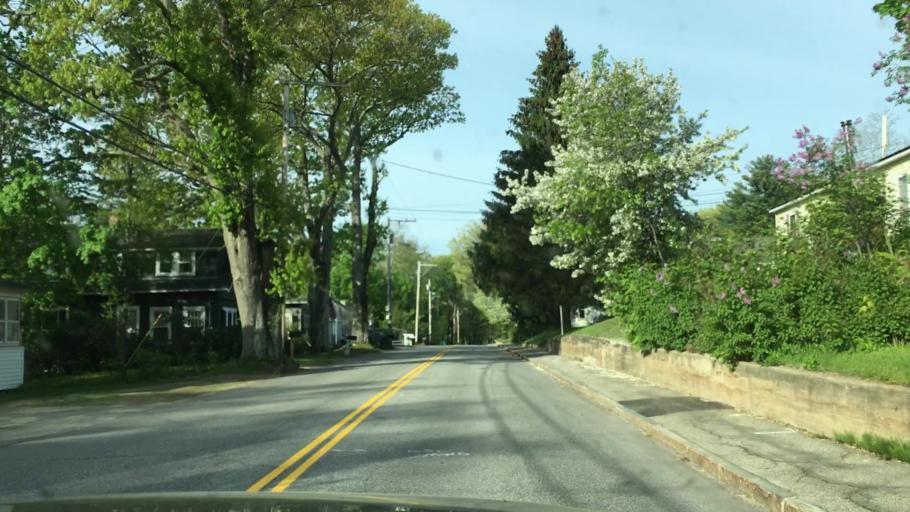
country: US
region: New Hampshire
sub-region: Belknap County
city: Meredith
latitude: 43.6522
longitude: -71.5017
